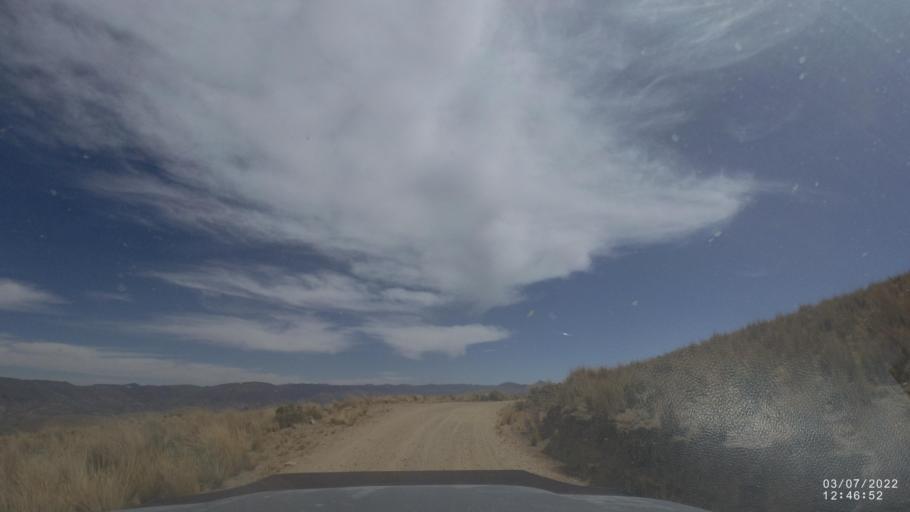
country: BO
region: Cochabamba
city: Irpa Irpa
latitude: -17.7714
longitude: -66.6397
